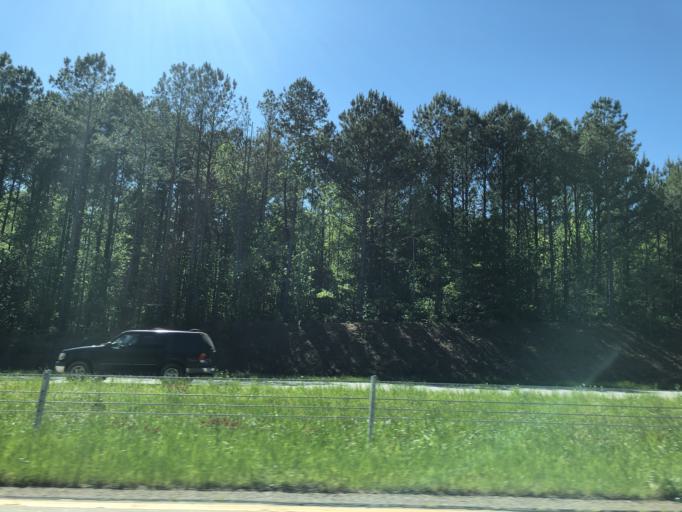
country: US
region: Georgia
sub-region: Oconee County
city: Bogart
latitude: 33.9327
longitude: -83.4671
